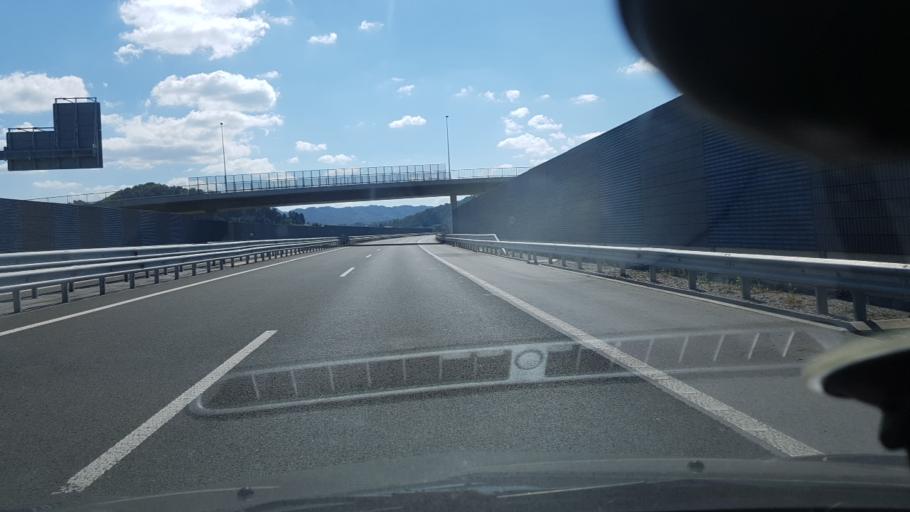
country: SI
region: Podlehnik
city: Podlehnik
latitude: 46.3599
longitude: 15.8679
